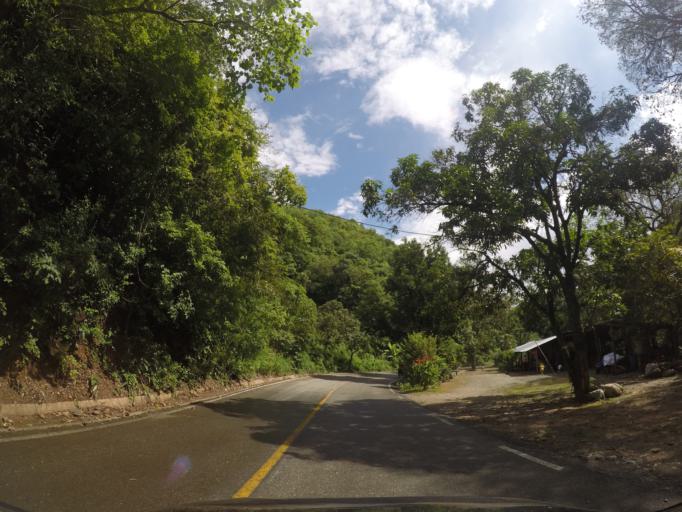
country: MX
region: Oaxaca
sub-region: San Jeronimo Coatlan
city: San Cristobal Honduras
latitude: 16.3614
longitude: -97.0904
